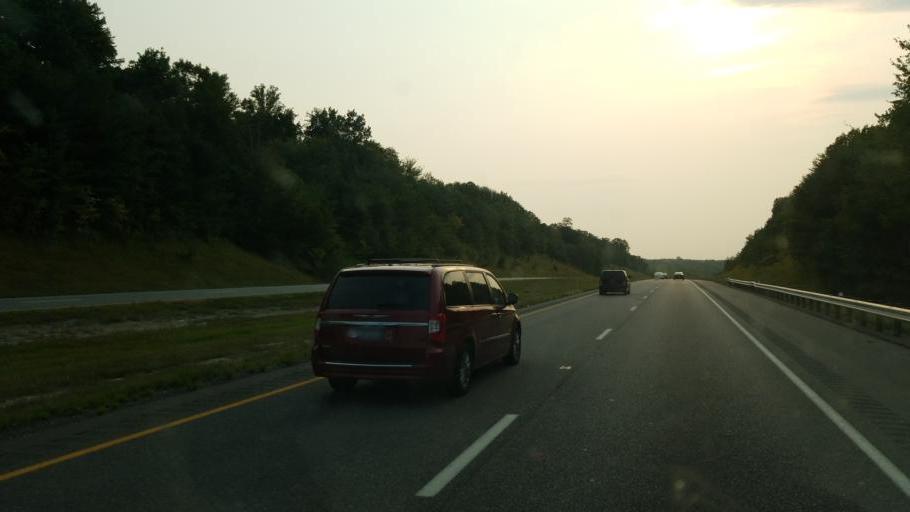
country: US
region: Ohio
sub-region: Geauga County
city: Bainbridge
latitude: 41.3888
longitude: -81.3715
